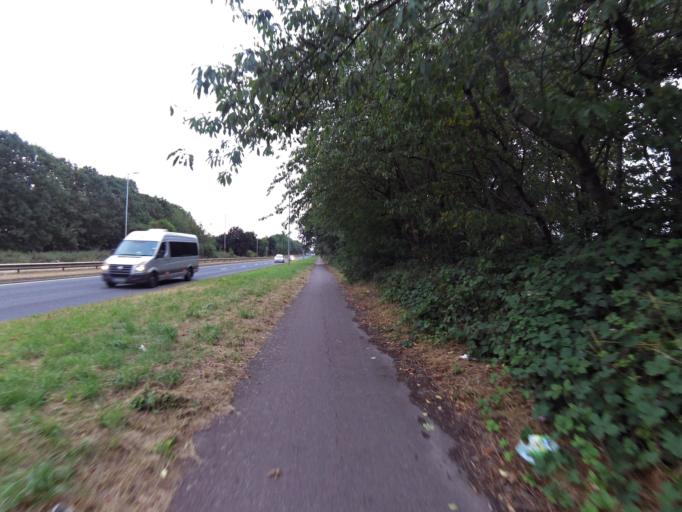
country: GB
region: England
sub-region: Hertfordshire
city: Shenley AV
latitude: 51.7373
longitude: -0.2800
